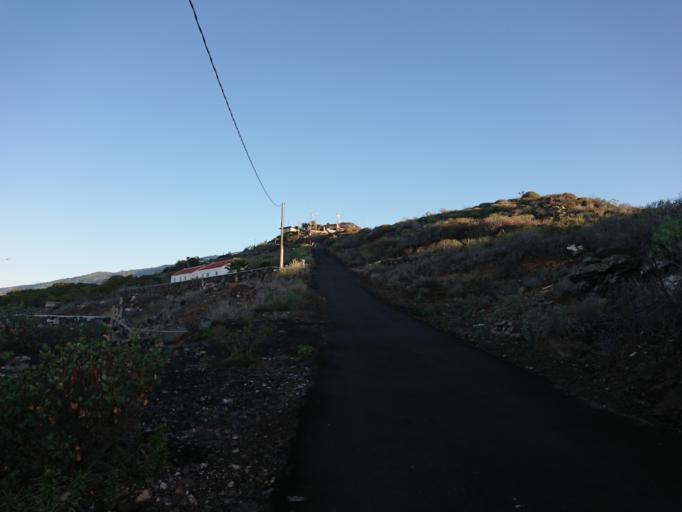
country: ES
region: Canary Islands
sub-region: Provincia de Santa Cruz de Tenerife
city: Tazacorte
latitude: 28.6607
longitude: -17.9435
